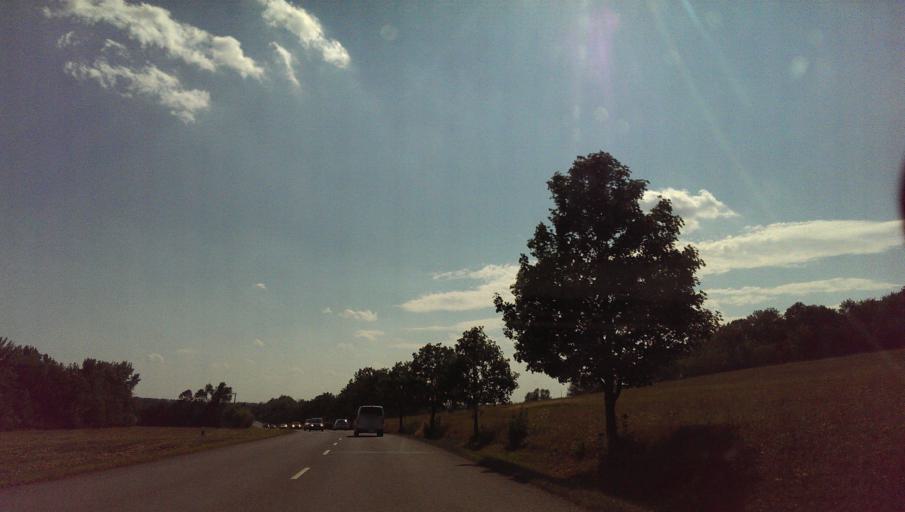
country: CZ
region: Zlin
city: Prusinovice
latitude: 49.3538
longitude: 17.6099
